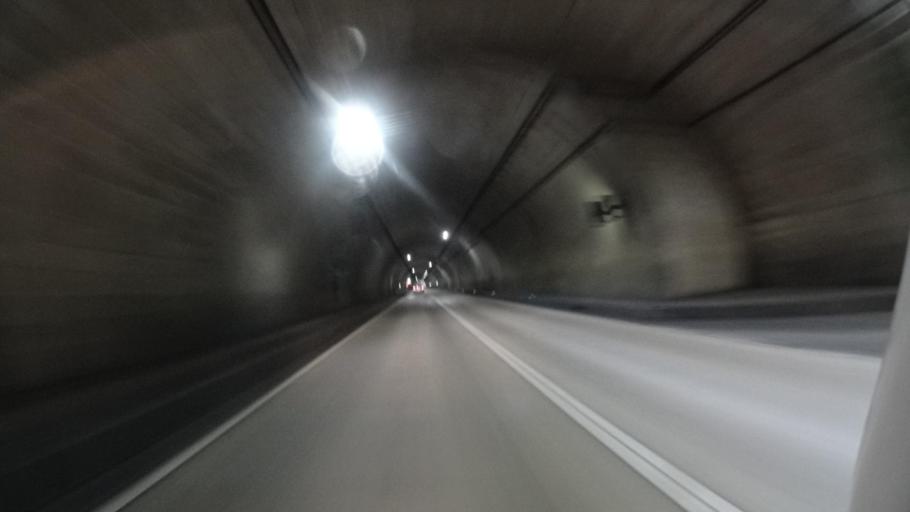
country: JP
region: Kyoto
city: Kameoka
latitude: 35.2271
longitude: 135.5734
